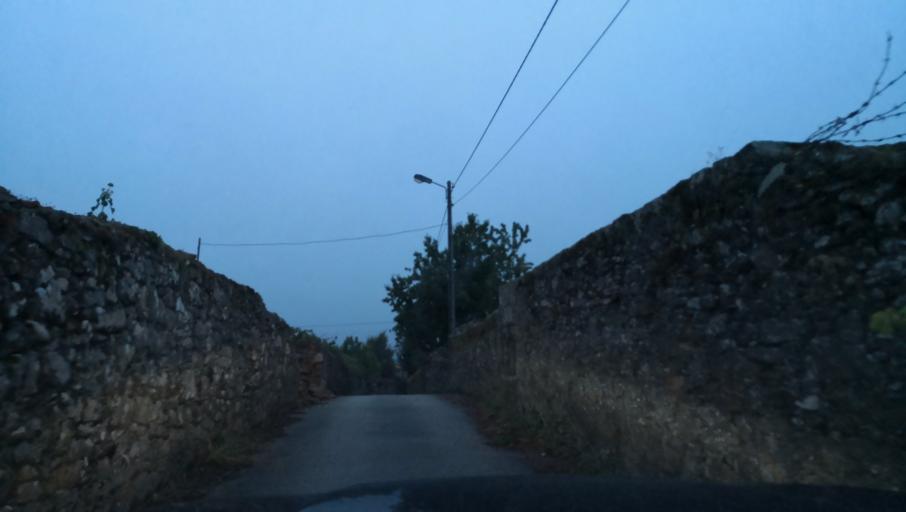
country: PT
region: Vila Real
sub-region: Sabrosa
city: Sabrosa
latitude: 41.2678
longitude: -7.6214
